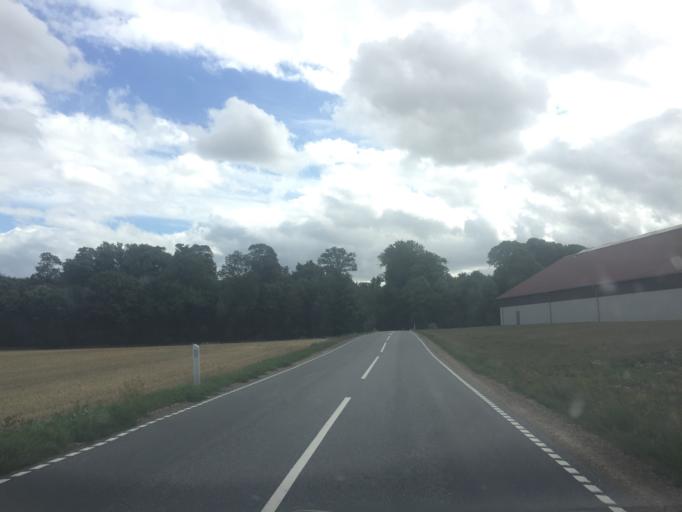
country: DK
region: Capital Region
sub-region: Egedal Kommune
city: Vekso
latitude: 55.6932
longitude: 12.2416
